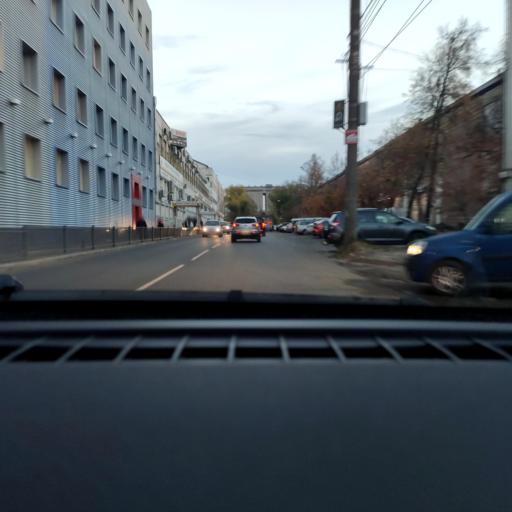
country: RU
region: Voronezj
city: Voronezh
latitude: 51.6807
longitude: 39.1723
